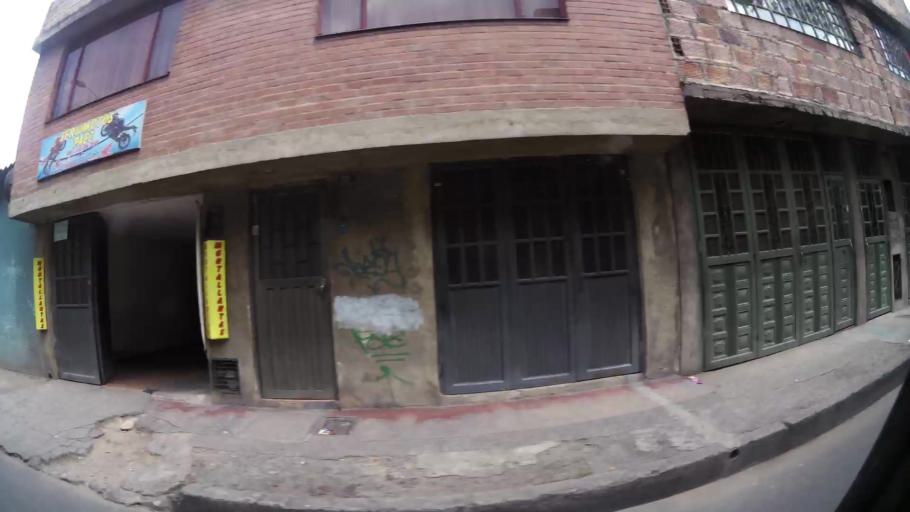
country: CO
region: Cundinamarca
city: Cota
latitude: 4.7289
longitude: -74.0907
